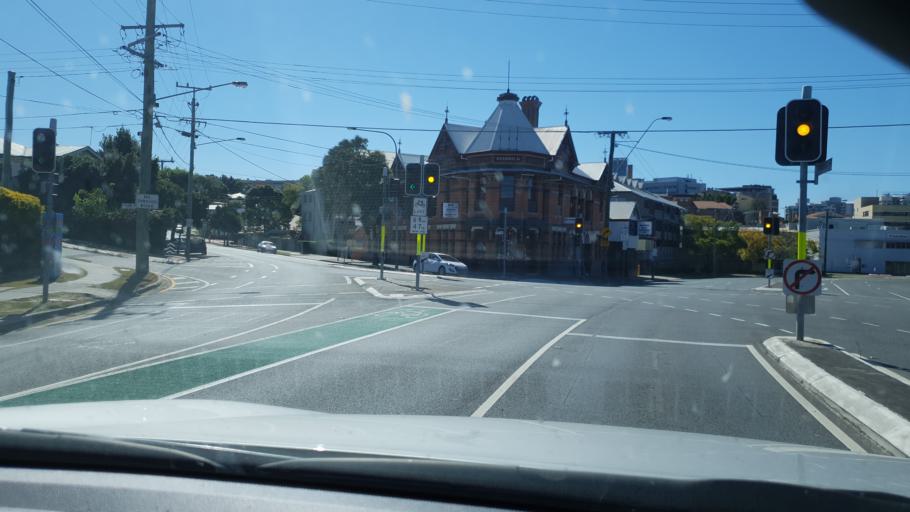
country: AU
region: Queensland
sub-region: Brisbane
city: Woolloongabba
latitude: -27.4903
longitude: 153.0271
